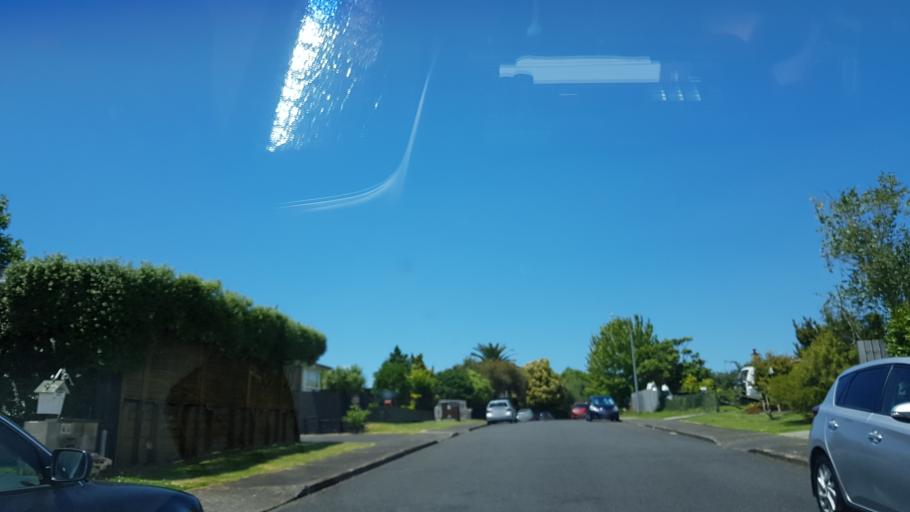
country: NZ
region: Auckland
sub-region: Auckland
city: North Shore
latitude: -36.7861
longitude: 174.6911
